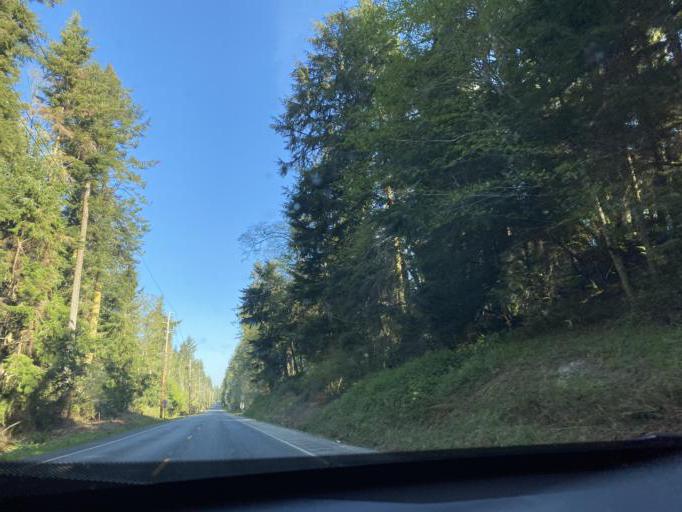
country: US
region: Washington
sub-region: Island County
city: Freeland
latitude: 48.0616
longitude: -122.5951
